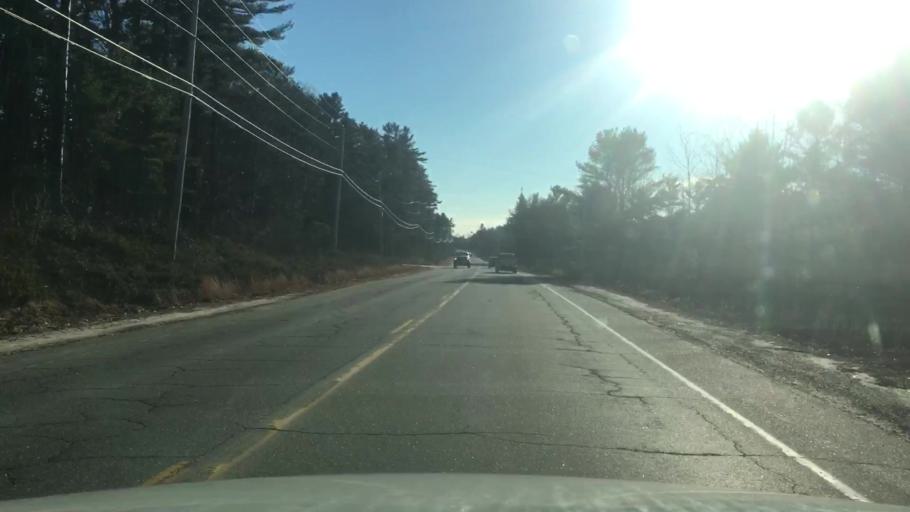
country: US
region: Maine
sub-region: Cumberland County
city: Brunswick
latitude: 43.8760
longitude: -69.9122
